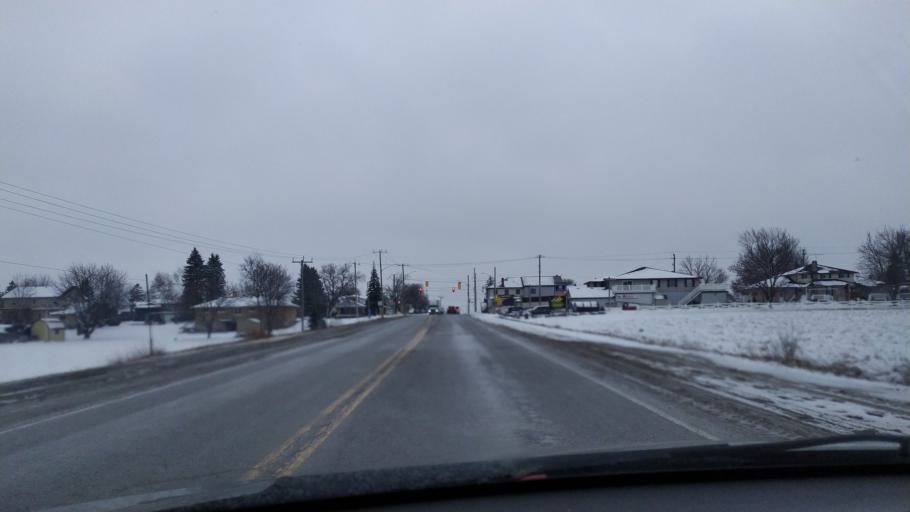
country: CA
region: Ontario
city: Waterloo
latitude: 43.6006
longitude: -80.6366
